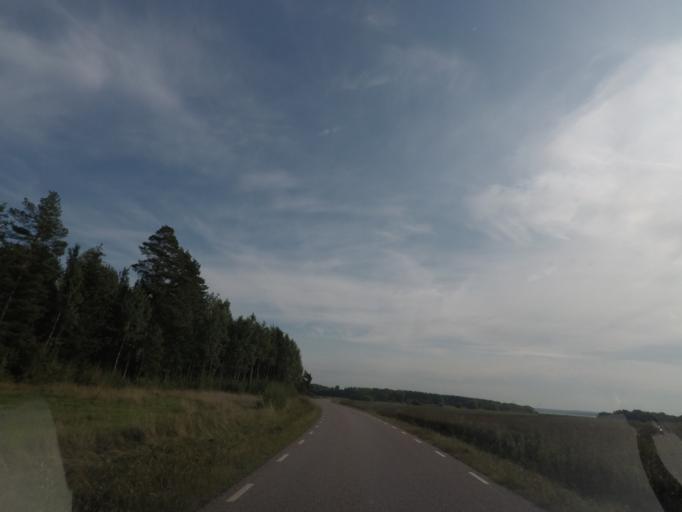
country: SE
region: Vaestmanland
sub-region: Kungsors Kommun
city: Kungsoer
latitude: 59.4939
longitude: 16.1542
